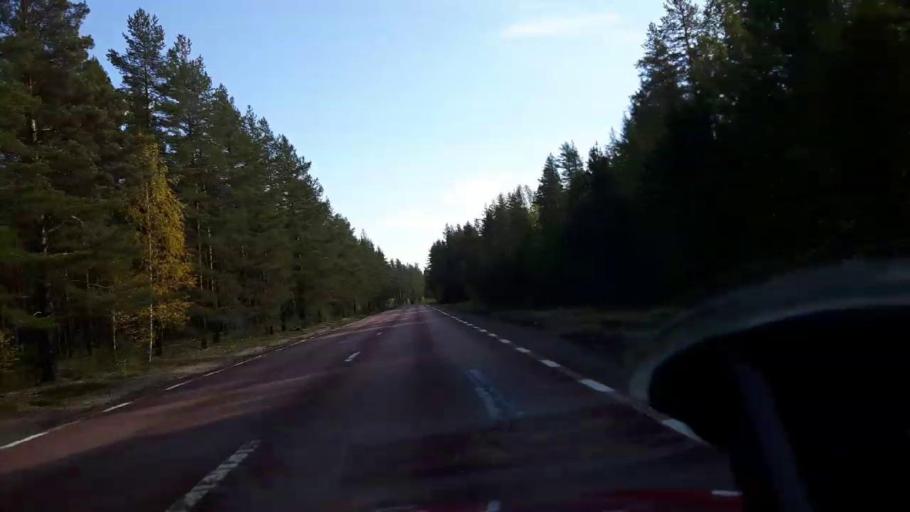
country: SE
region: Gaevleborg
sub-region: Ljusdals Kommun
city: Farila
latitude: 61.9242
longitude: 15.5915
